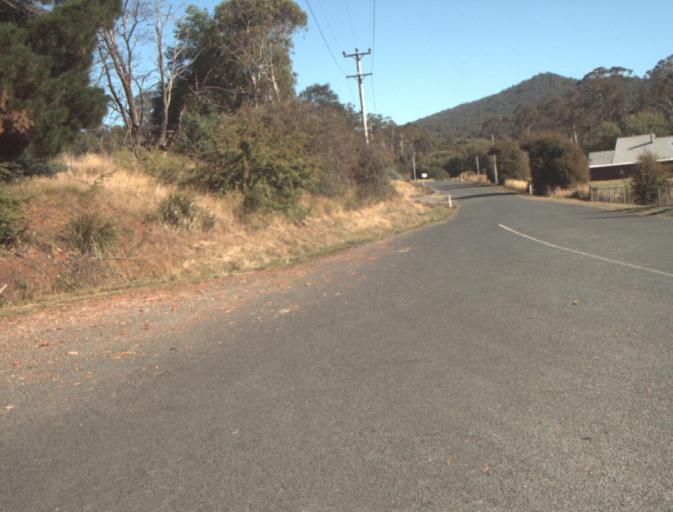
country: AU
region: Tasmania
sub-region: Launceston
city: Newstead
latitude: -41.3909
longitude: 147.2977
